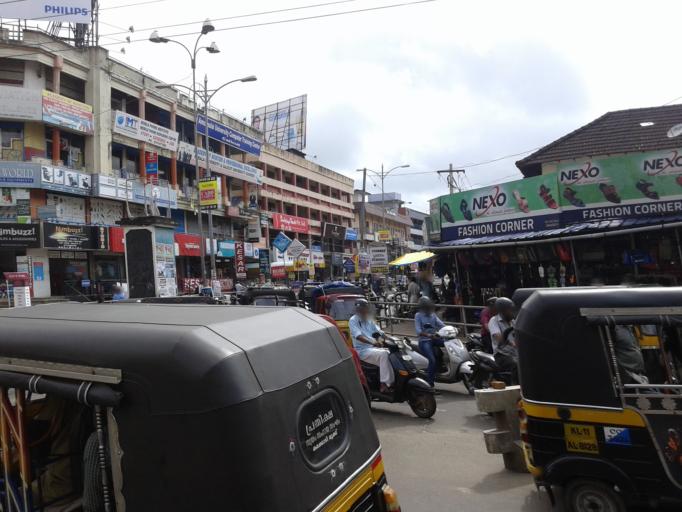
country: IN
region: Kerala
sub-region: Kozhikode
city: Kozhikode
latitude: 11.2469
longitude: 75.7846
